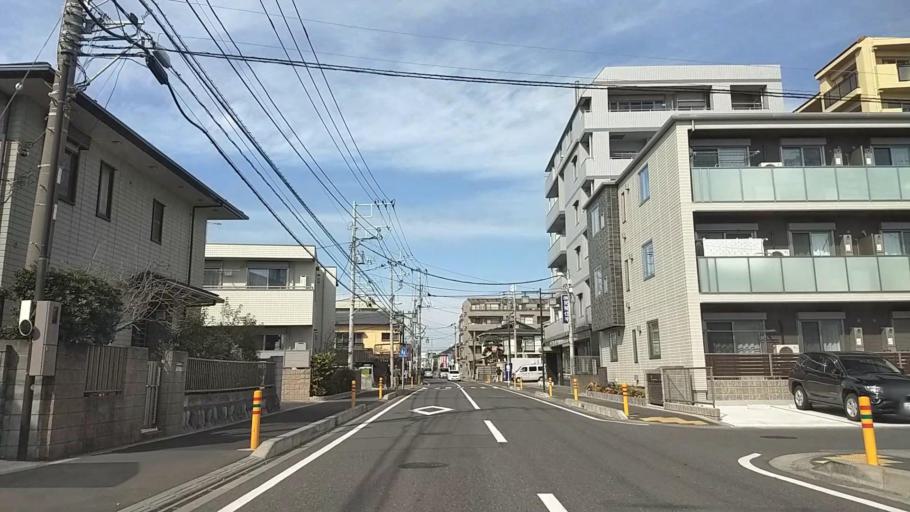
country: JP
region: Kanagawa
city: Chigasaki
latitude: 35.3286
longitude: 139.4380
